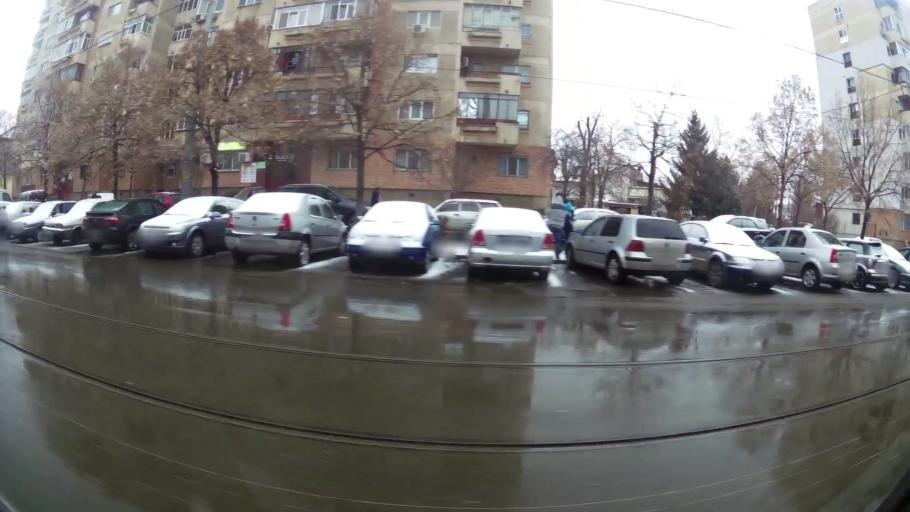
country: RO
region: Prahova
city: Ploiesti
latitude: 44.9434
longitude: 26.0265
